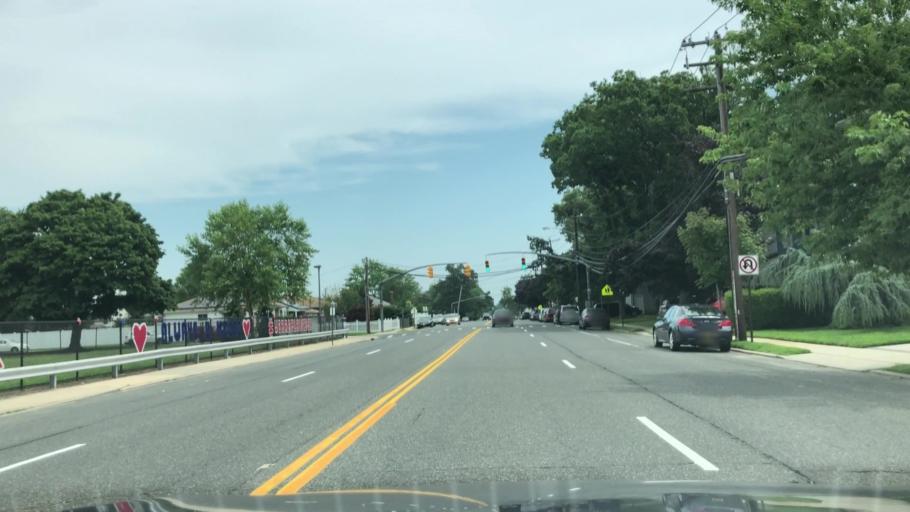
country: US
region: New York
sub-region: Nassau County
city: Massapequa
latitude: 40.6917
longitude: -73.4756
